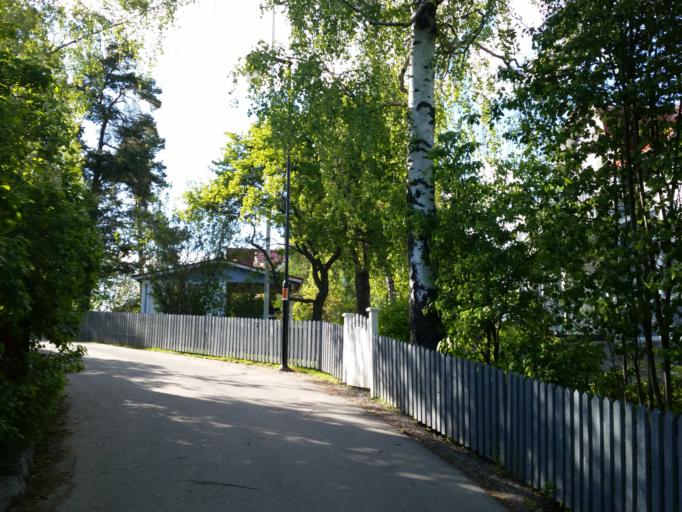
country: SE
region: Stockholm
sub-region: Sundbybergs Kommun
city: Sundbyberg
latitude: 59.3731
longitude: 17.9600
